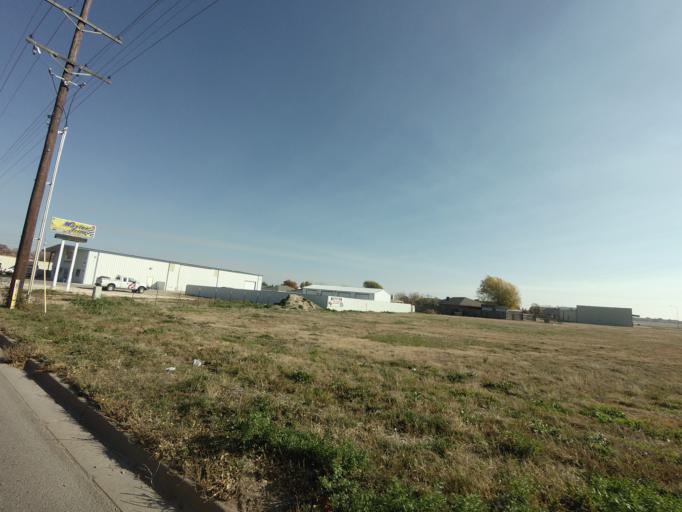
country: US
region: New Mexico
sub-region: Curry County
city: Clovis
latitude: 34.4054
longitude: -103.1788
